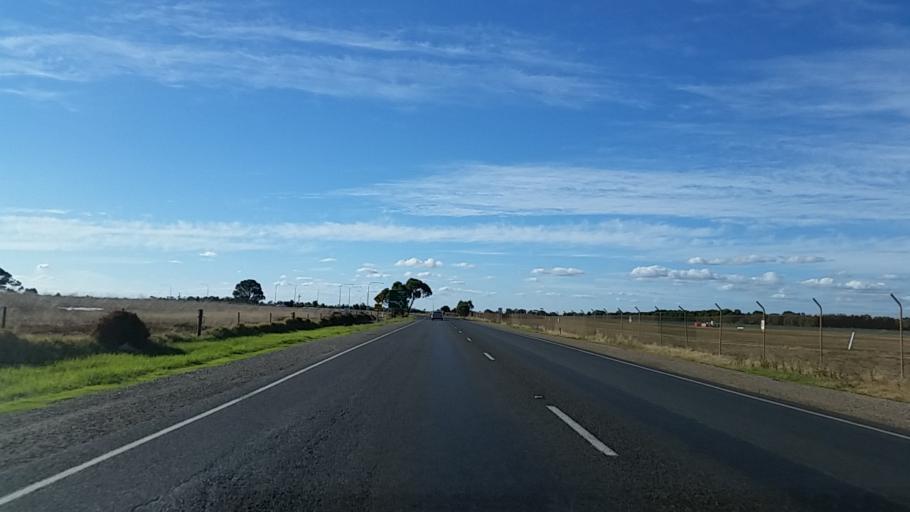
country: AU
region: South Australia
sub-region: Playford
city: Virginia
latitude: -34.6961
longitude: 138.6136
